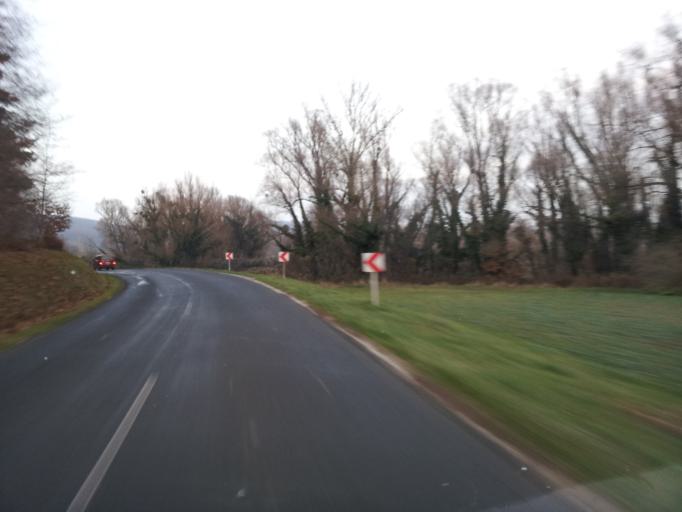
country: HU
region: Zala
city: Heviz
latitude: 46.8688
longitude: 17.1549
